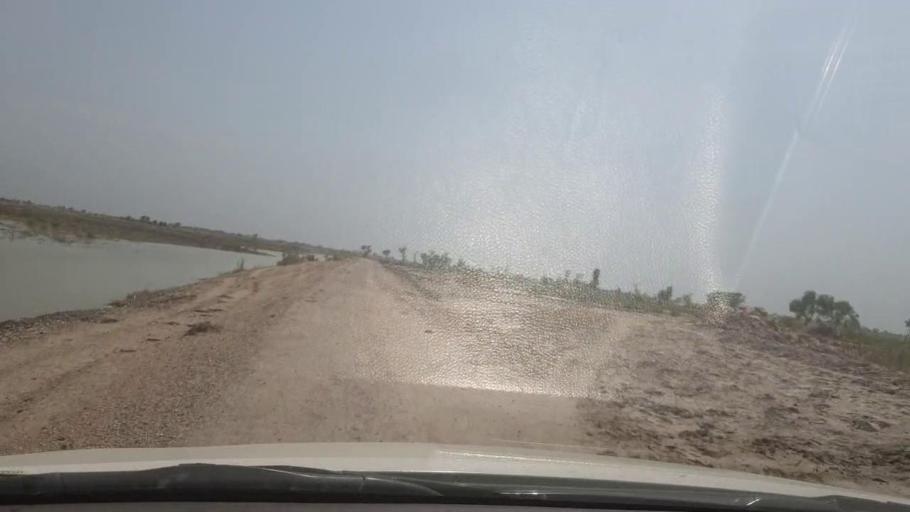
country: PK
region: Sindh
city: Shikarpur
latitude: 28.0342
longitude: 68.5736
